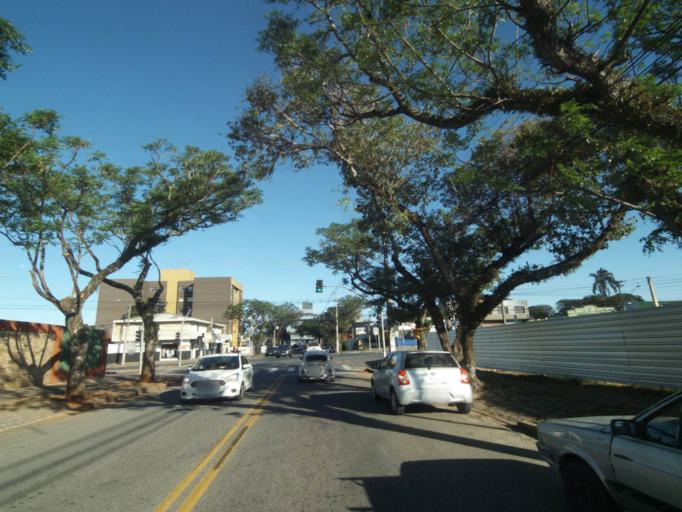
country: BR
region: Parana
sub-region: Curitiba
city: Curitiba
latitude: -25.3917
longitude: -49.2394
